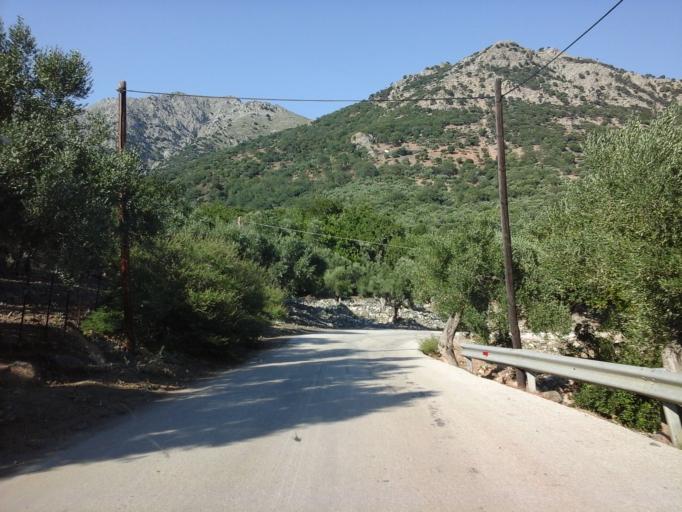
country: GR
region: East Macedonia and Thrace
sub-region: Nomos Evrou
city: Samothraki
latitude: 40.4127
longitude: 25.5594
